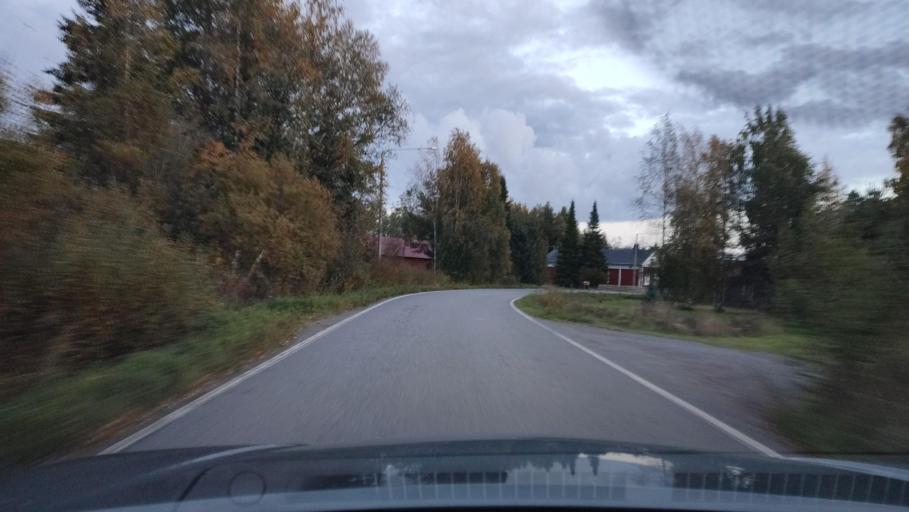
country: FI
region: Ostrobothnia
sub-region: Sydosterbotten
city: Kristinestad
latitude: 62.2644
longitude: 21.5277
